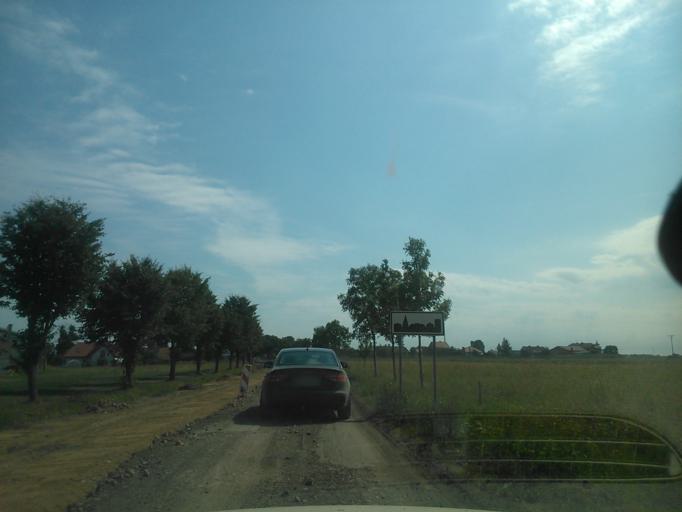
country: PL
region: Warmian-Masurian Voivodeship
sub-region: Powiat dzialdowski
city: Dzialdowo
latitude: 53.2217
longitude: 20.2071
